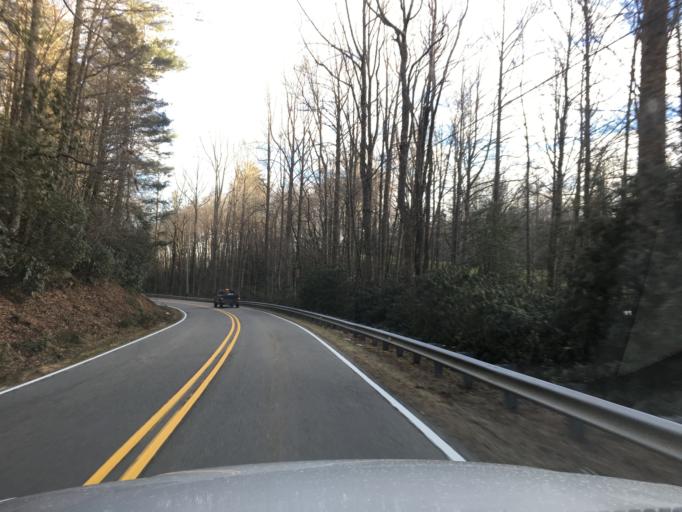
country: US
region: North Carolina
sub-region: Jackson County
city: Cullowhee
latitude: 35.1150
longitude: -82.9936
